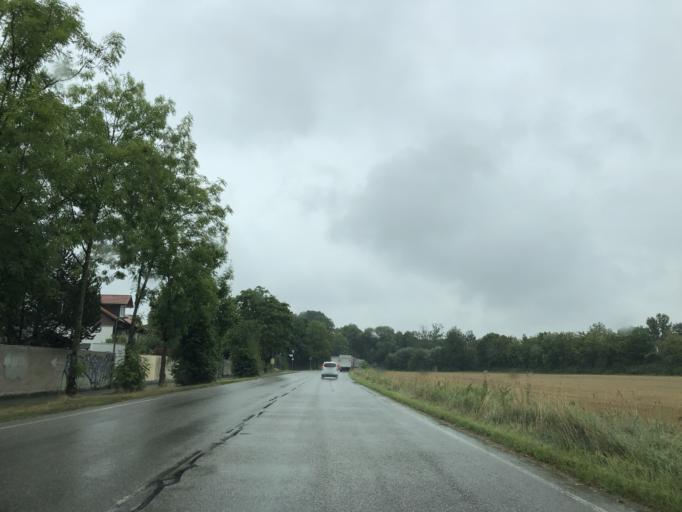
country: DE
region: Bavaria
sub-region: Upper Bavaria
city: Garching bei Munchen
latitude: 48.2408
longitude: 11.6536
